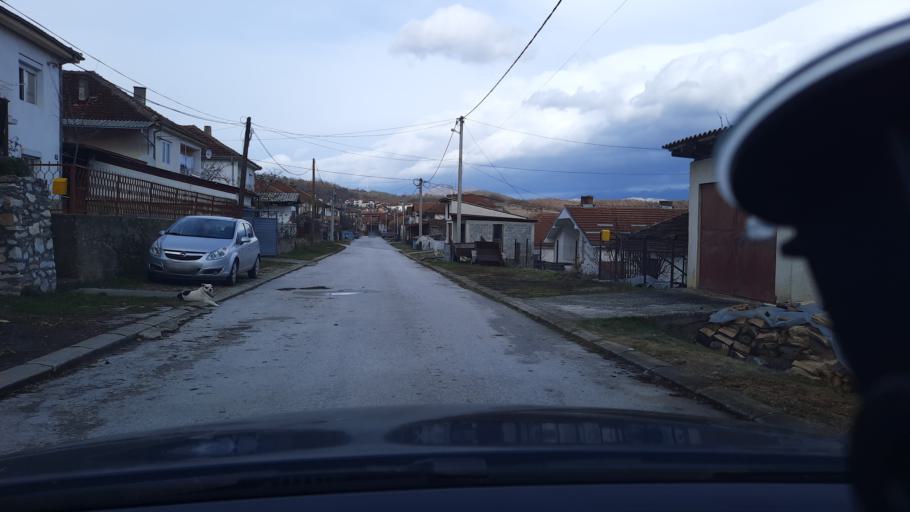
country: MK
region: Makedonski Brod
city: Makedonski Brod
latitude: 41.5105
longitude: 21.2144
